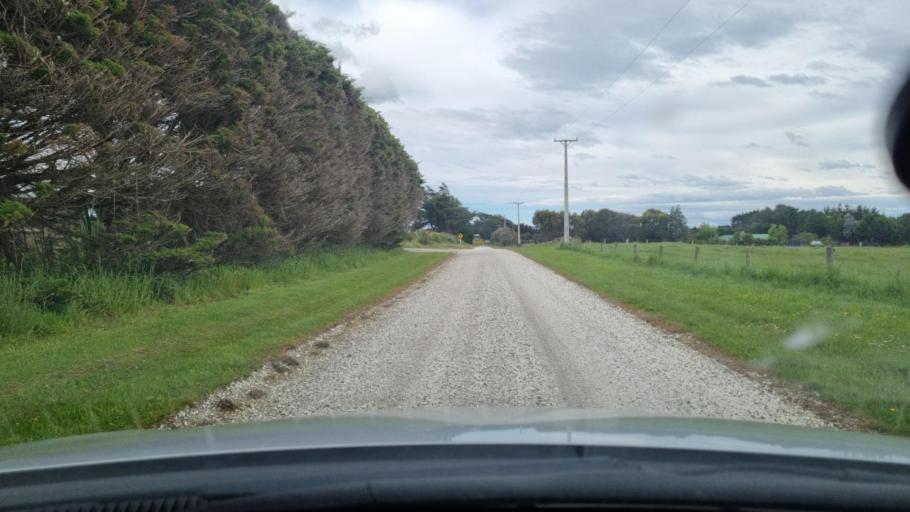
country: NZ
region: Southland
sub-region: Invercargill City
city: Invercargill
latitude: -46.4061
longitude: 168.2598
